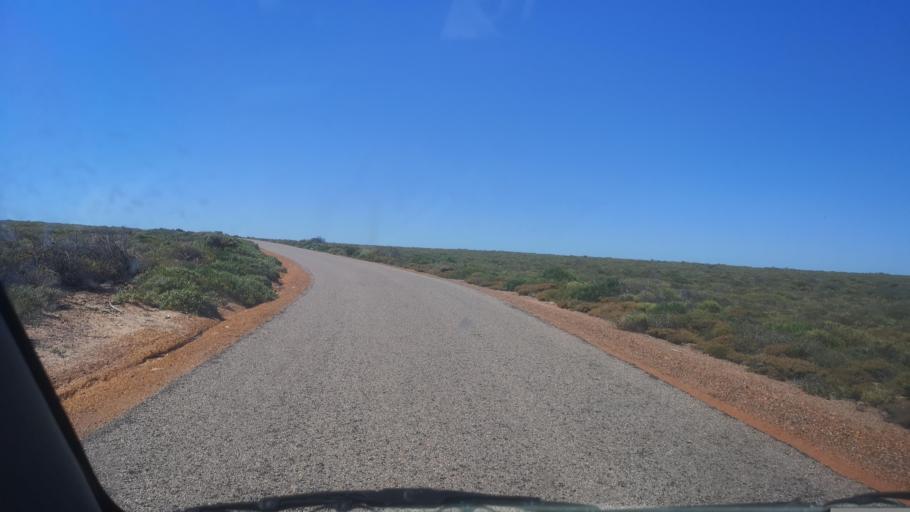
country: AU
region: Western Australia
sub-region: Northampton Shire
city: Kalbarri
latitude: -27.8270
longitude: 114.1163
